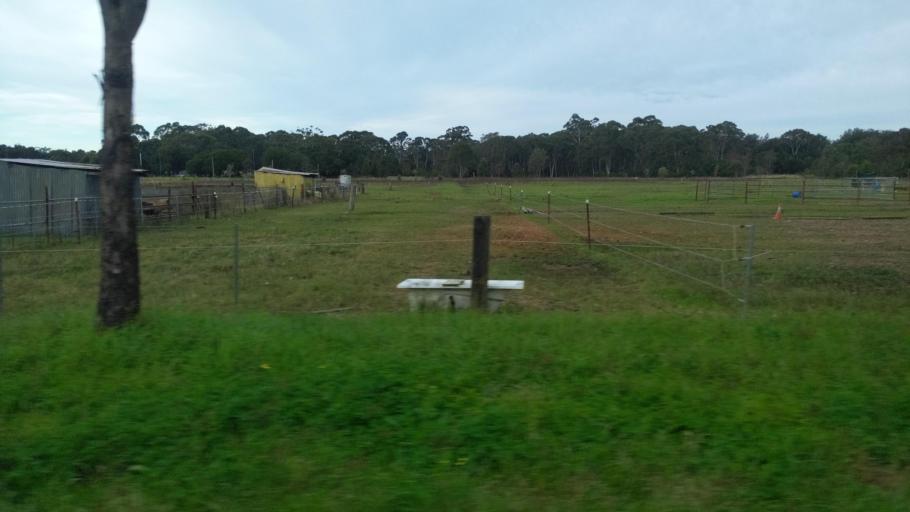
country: AU
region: New South Wales
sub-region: Blacktown
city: Glendenning
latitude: -33.7342
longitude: 150.8648
